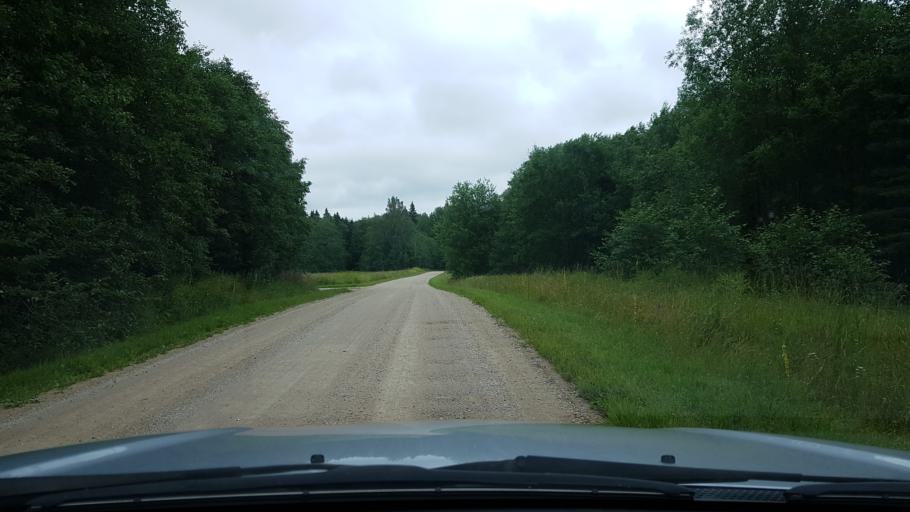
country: EE
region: Ida-Virumaa
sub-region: Narva-Joesuu linn
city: Narva-Joesuu
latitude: 59.3599
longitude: 28.0426
